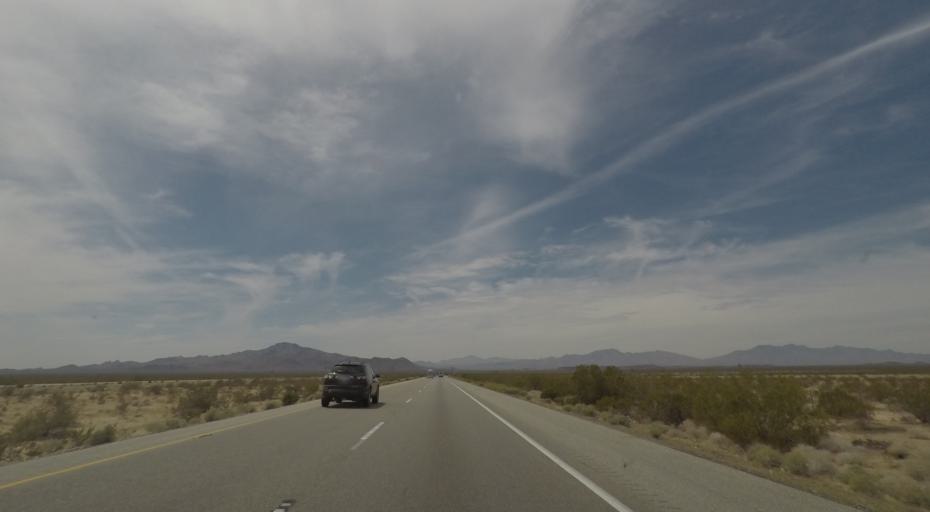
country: US
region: California
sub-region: San Bernardino County
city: Needles
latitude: 34.8091
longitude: -115.2259
